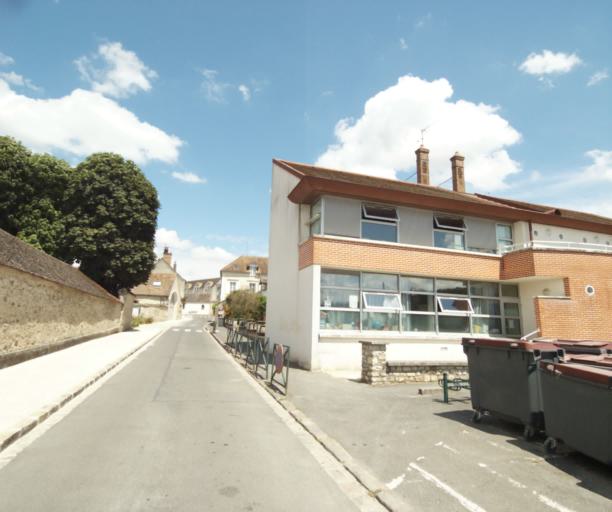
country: FR
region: Ile-de-France
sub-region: Departement de Seine-et-Marne
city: Hericy
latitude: 48.4487
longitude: 2.7647
